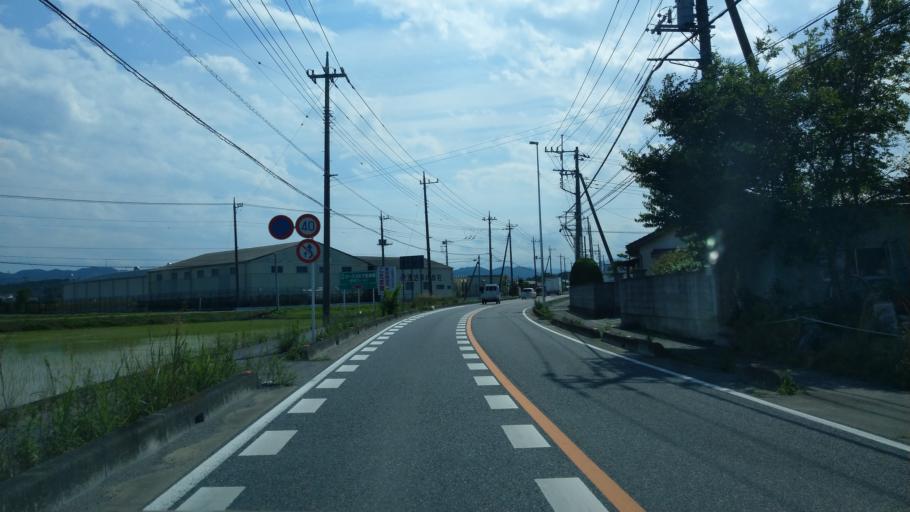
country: JP
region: Saitama
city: Kodamacho-kodamaminami
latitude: 36.2130
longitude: 139.1562
